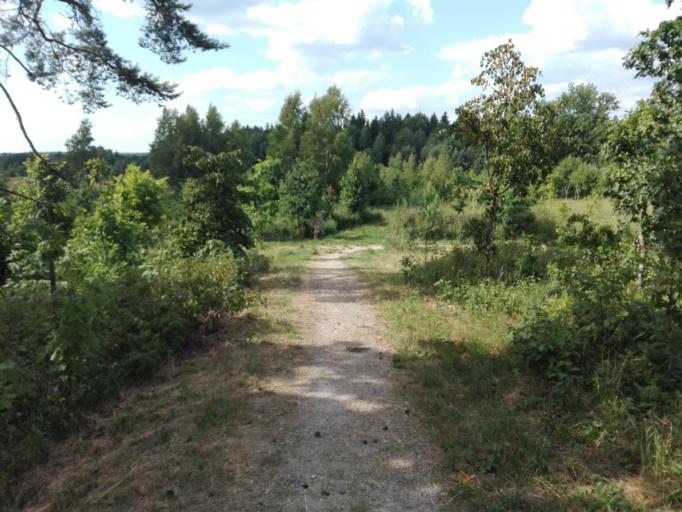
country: LT
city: Skaidiskes
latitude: 54.5316
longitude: 25.6281
